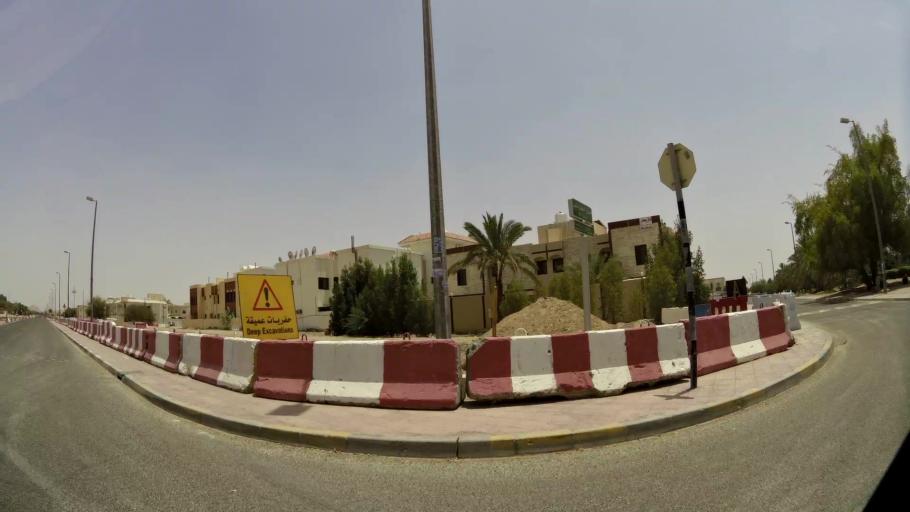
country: AE
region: Abu Dhabi
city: Al Ain
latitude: 24.2106
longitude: 55.7160
